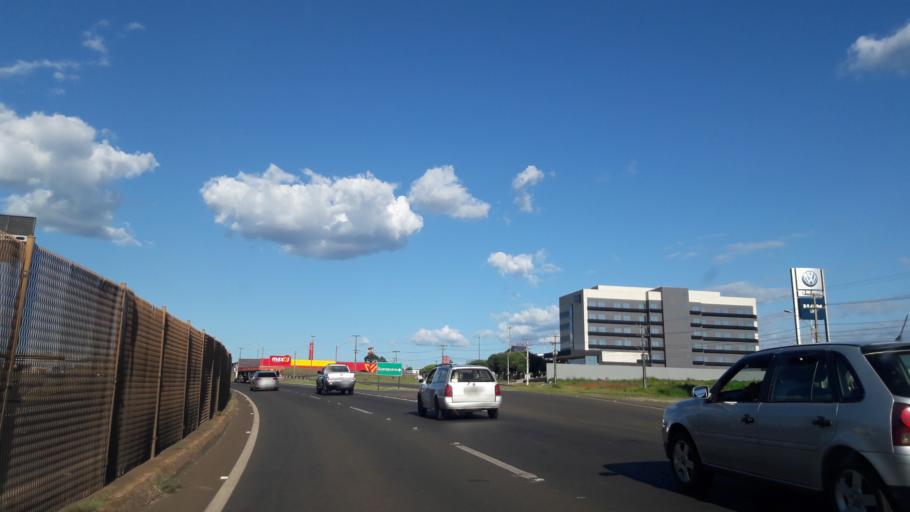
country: BR
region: Parana
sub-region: Guarapuava
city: Guarapuava
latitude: -25.3657
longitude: -51.4788
